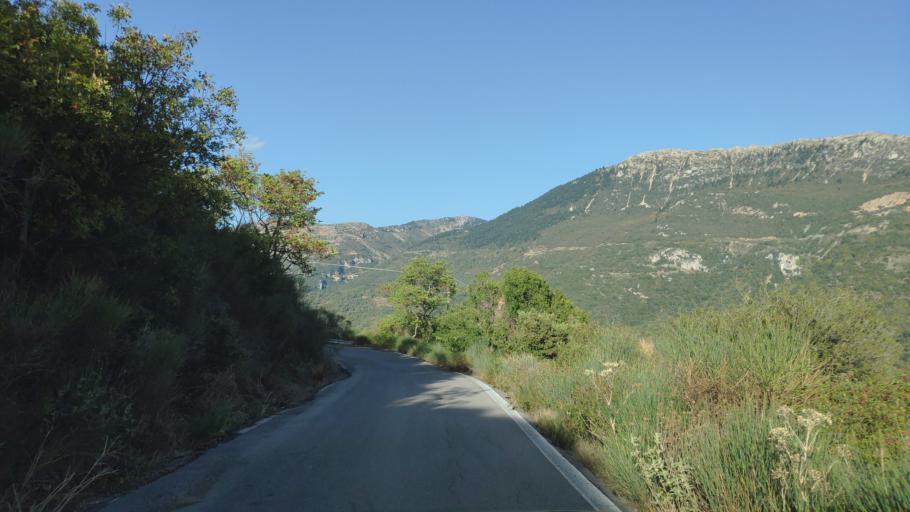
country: GR
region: Peloponnese
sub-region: Nomos Arkadias
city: Dimitsana
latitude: 37.5561
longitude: 22.0400
